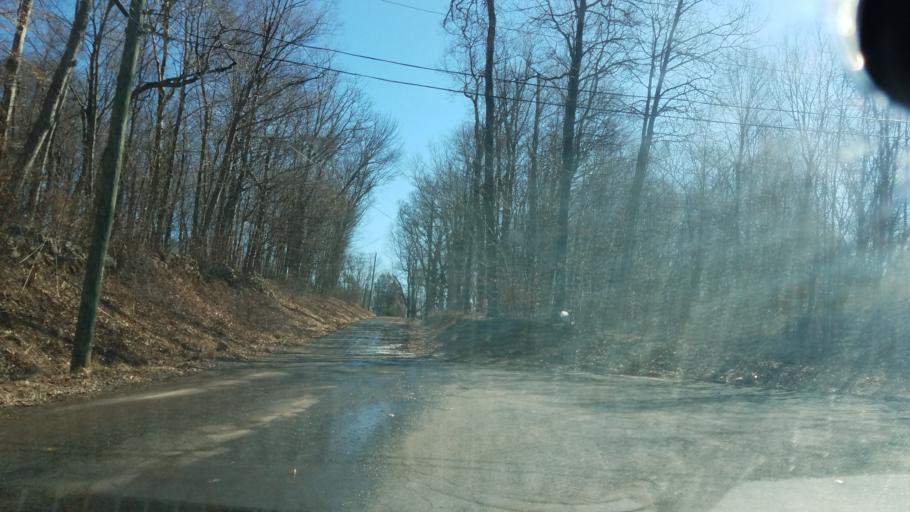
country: US
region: Connecticut
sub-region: Middlesex County
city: East Hampton
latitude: 41.5879
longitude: -72.4711
